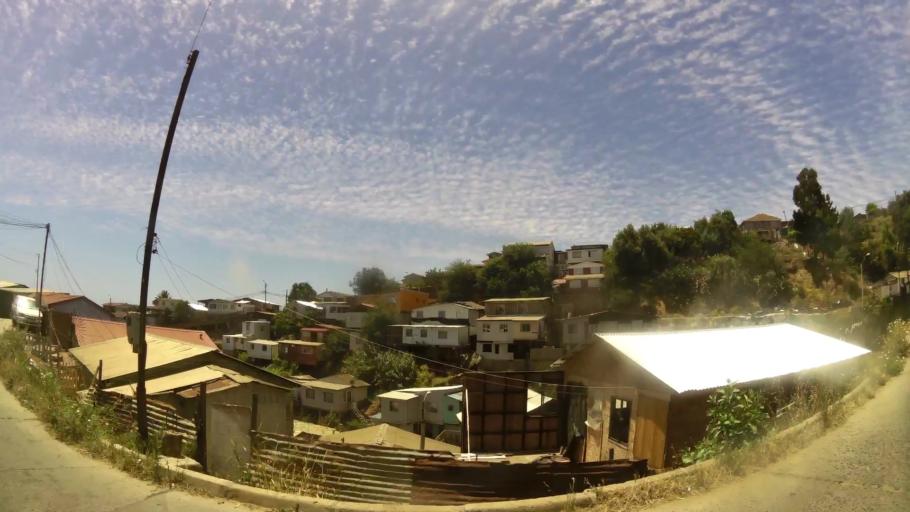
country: CL
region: Valparaiso
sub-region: Provincia de Valparaiso
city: Vina del Mar
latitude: -33.0440
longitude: -71.5855
